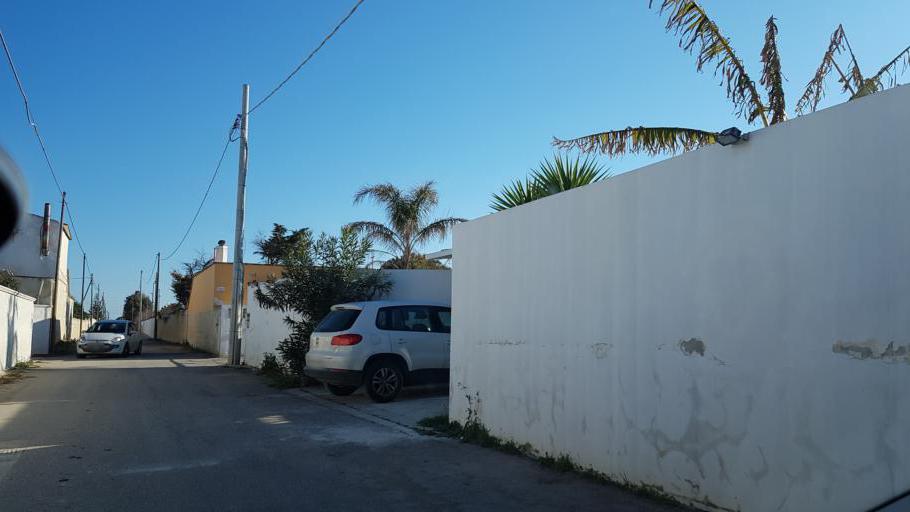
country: IT
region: Apulia
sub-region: Provincia di Brindisi
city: Materdomini
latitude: 40.6748
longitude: 17.9410
